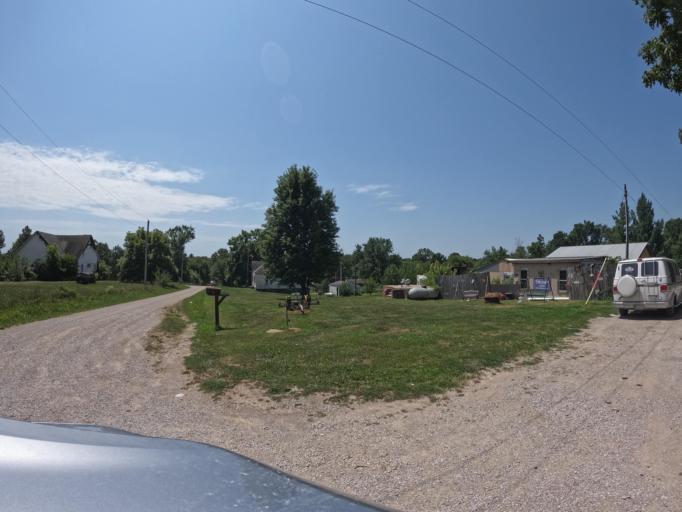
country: US
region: Iowa
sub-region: Appanoose County
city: Centerville
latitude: 40.7783
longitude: -92.9523
